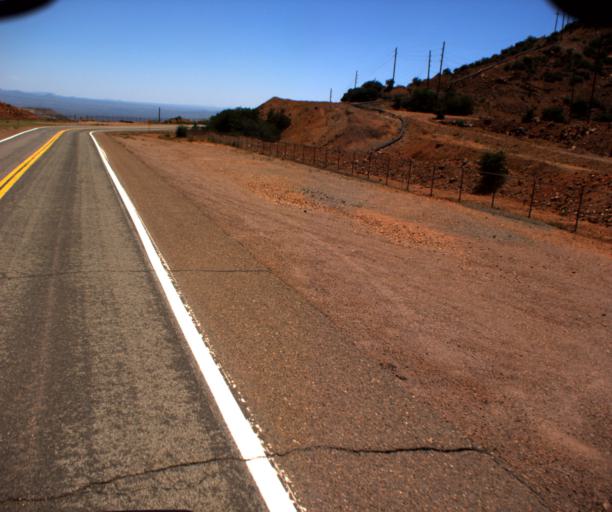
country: US
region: Arizona
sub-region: Greenlee County
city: Morenci
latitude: 33.0984
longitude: -109.3801
